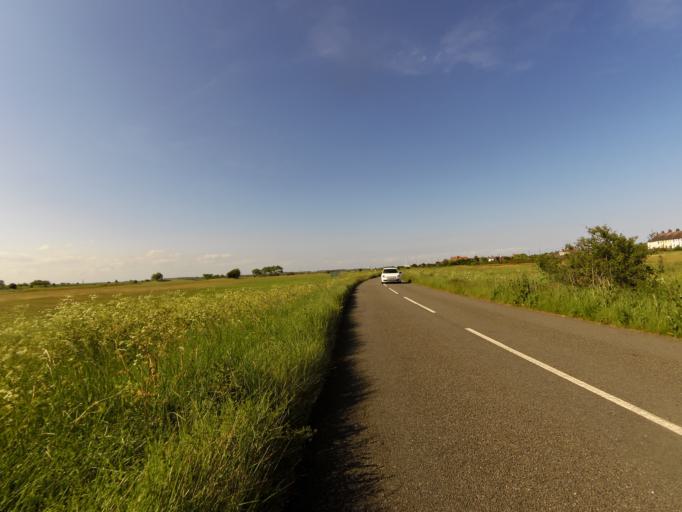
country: GB
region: England
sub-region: Suffolk
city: Felixstowe
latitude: 51.9850
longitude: 1.3867
